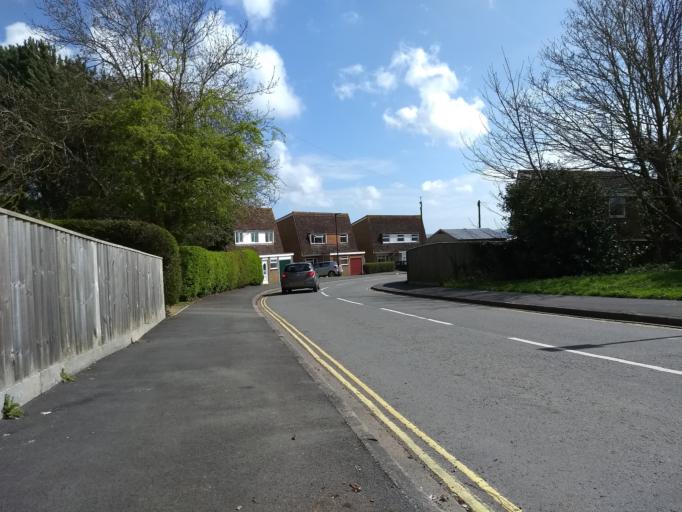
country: GB
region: England
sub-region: Isle of Wight
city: East Cowes
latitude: 50.7295
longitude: -1.2341
